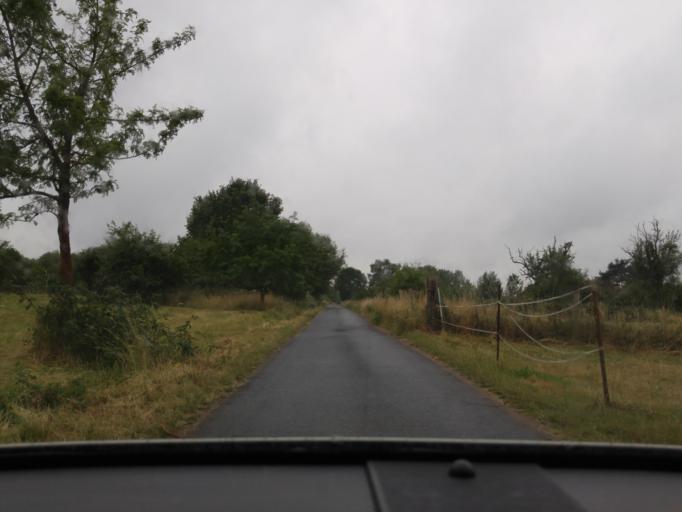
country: DE
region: Hesse
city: Dreieich
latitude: 50.0169
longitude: 8.7132
